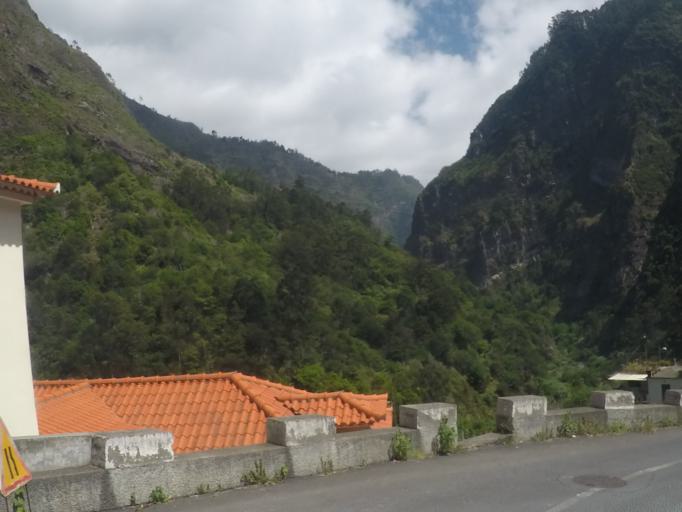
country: PT
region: Madeira
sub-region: Camara de Lobos
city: Curral das Freiras
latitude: 32.7076
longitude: -16.9720
